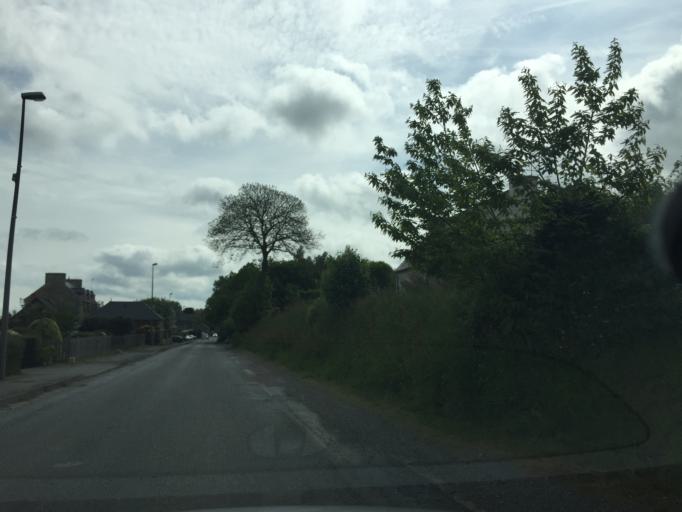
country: FR
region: Brittany
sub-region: Departement des Cotes-d'Armor
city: Corseul
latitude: 48.5111
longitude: -2.1324
